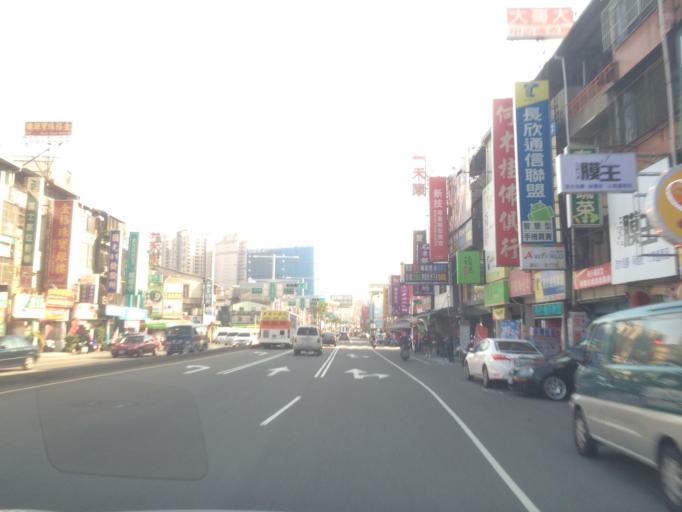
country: TW
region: Taiwan
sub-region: Taichung City
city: Taichung
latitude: 24.1778
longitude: 120.6689
